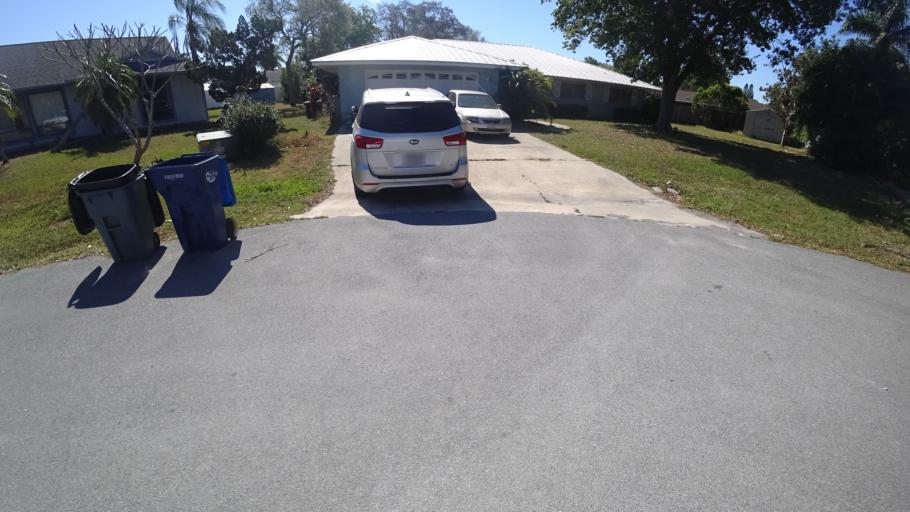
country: US
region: Florida
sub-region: Manatee County
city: West Bradenton
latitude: 27.4798
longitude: -82.6391
